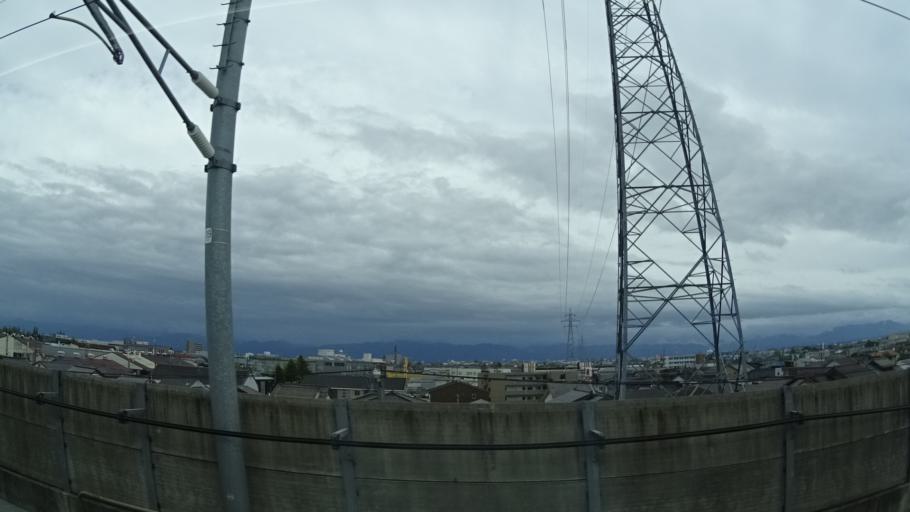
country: JP
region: Toyama
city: Toyama-shi
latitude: 36.7022
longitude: 137.2346
